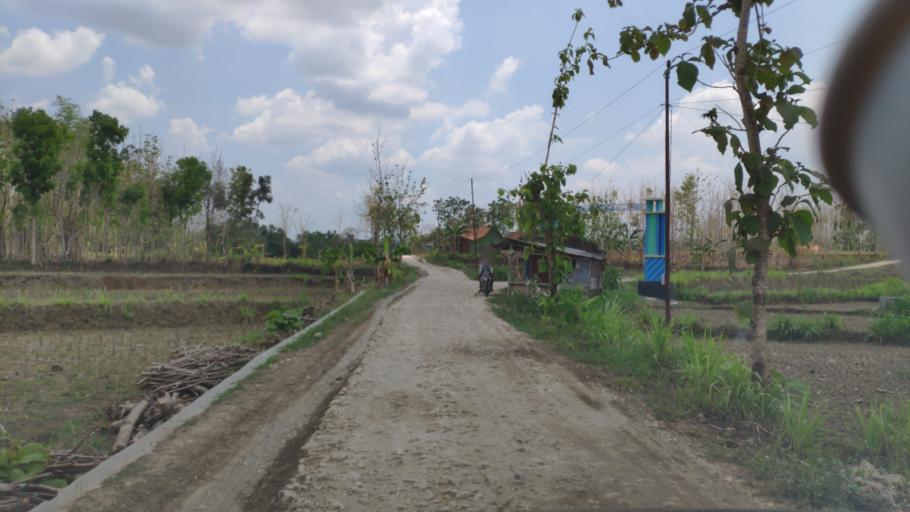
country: ID
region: Central Java
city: Bacem
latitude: -7.0551
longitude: 111.3708
